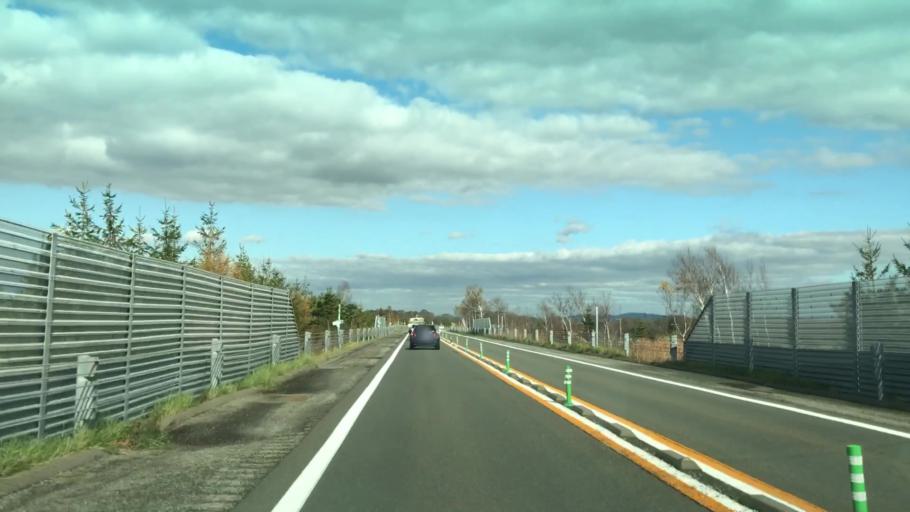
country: JP
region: Hokkaido
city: Chitose
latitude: 42.8779
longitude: 141.6179
